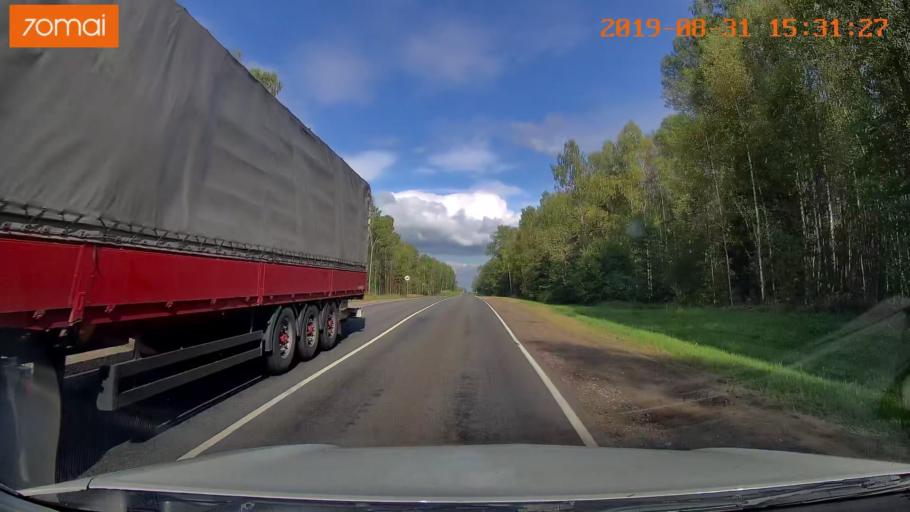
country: RU
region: Kaluga
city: Baryatino
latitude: 54.5826
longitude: 34.6554
